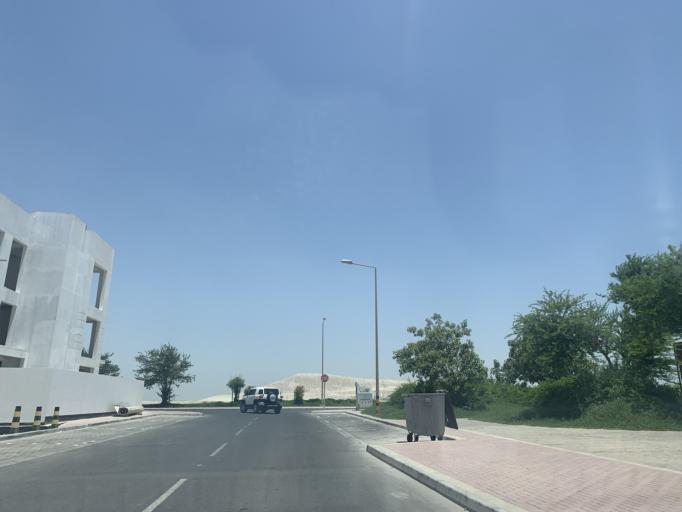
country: BH
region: Manama
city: Jidd Hafs
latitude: 26.2387
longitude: 50.4698
